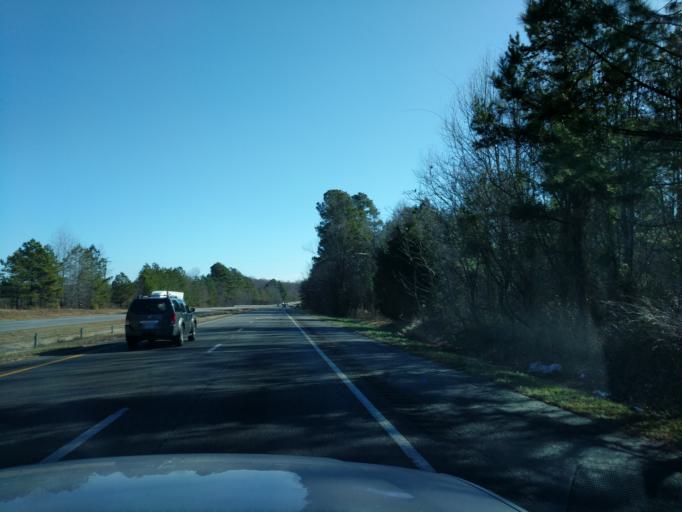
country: US
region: South Carolina
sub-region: Greenville County
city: Fountain Inn
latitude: 34.6372
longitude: -82.1283
